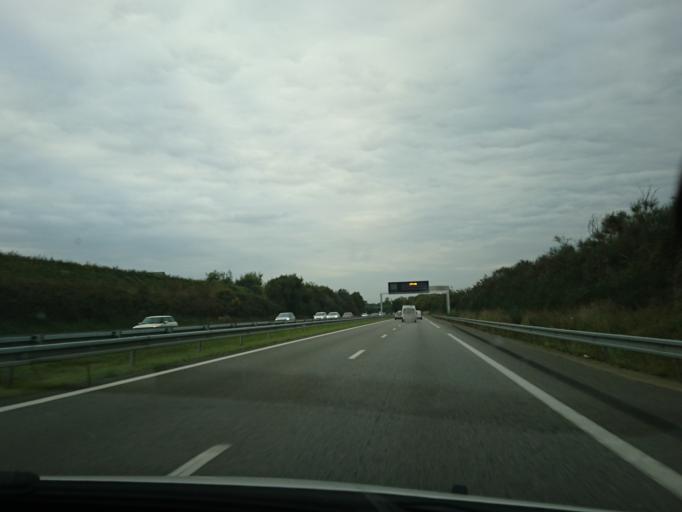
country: FR
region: Brittany
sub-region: Departement du Morbihan
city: Theix
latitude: 47.6262
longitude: -2.6336
